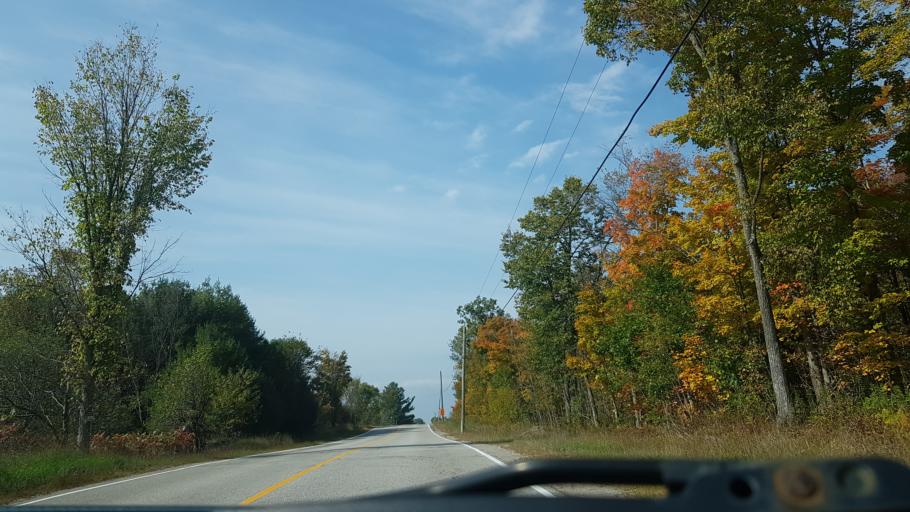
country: CA
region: Ontario
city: Gravenhurst
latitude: 44.7797
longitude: -79.2749
